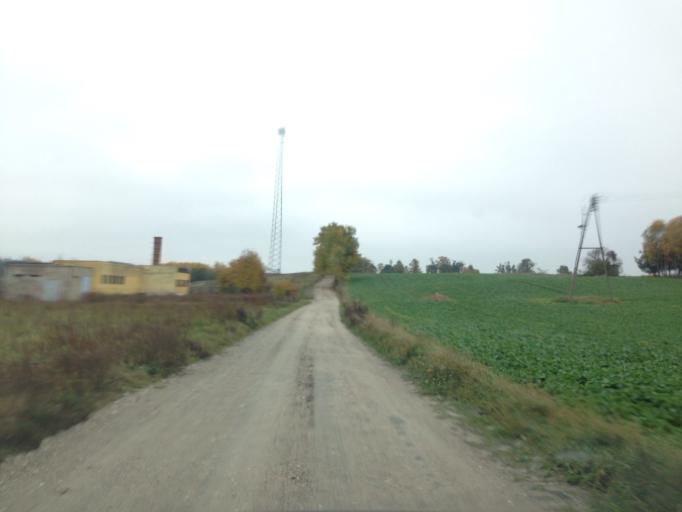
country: PL
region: Kujawsko-Pomorskie
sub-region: Powiat brodnicki
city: Gorzno
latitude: 53.2012
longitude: 19.6319
